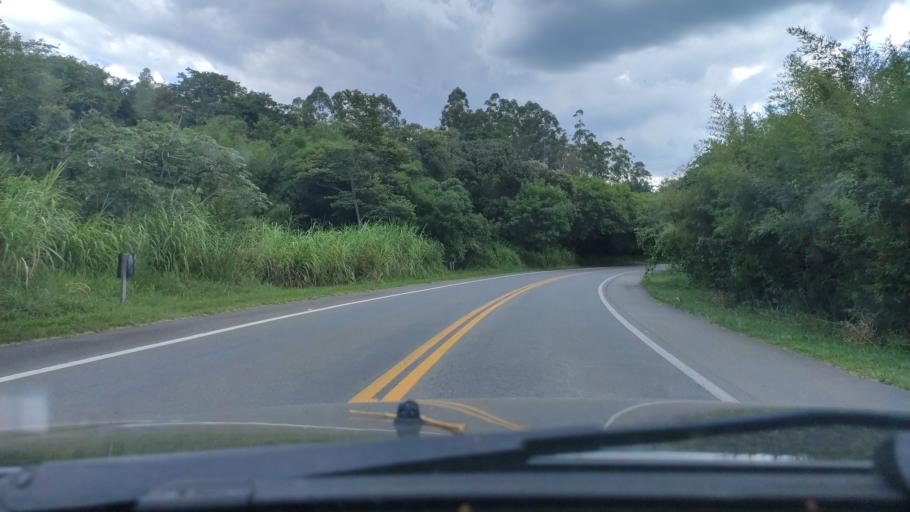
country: BR
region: Sao Paulo
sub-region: Aguas De Lindoia
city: Aguas de Lindoia
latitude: -22.4727
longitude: -46.6969
